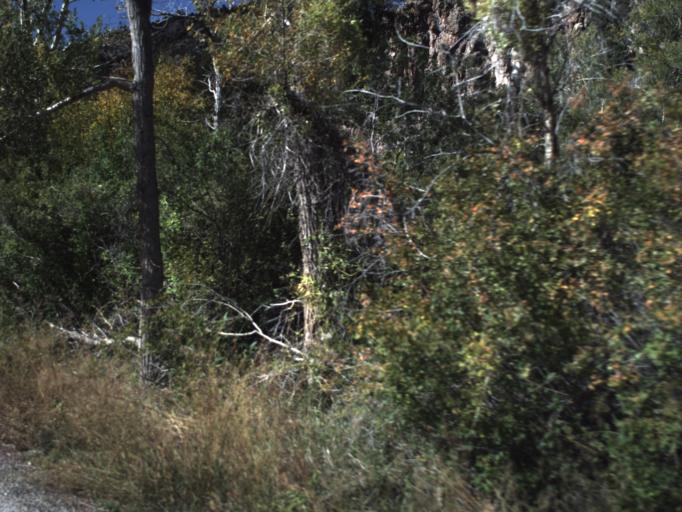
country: US
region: Utah
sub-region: Beaver County
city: Beaver
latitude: 38.2796
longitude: -112.5665
